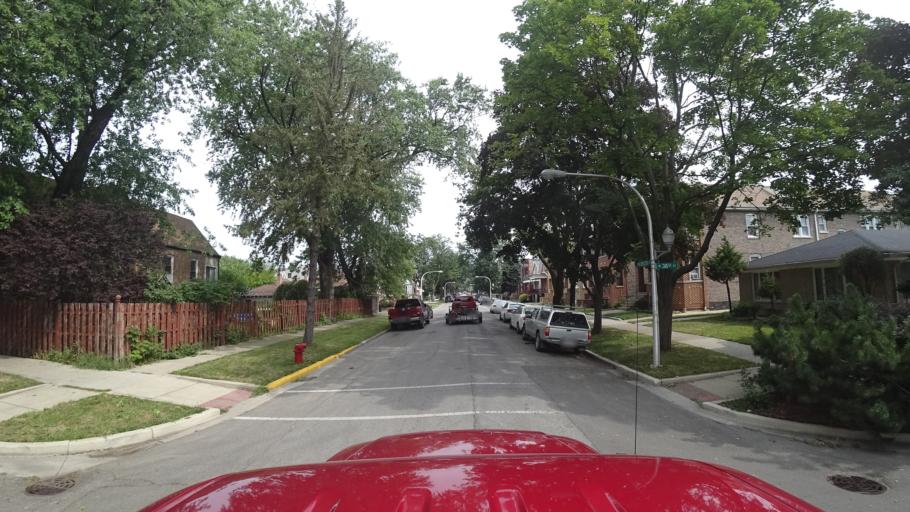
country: US
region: Illinois
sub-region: Cook County
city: Chicago
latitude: 41.8250
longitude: -87.6740
